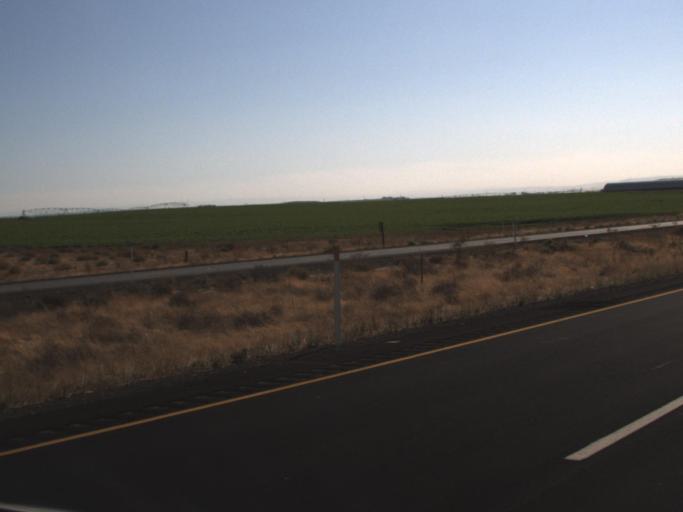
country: US
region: Washington
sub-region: Franklin County
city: Pasco
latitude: 46.2837
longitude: -119.0934
